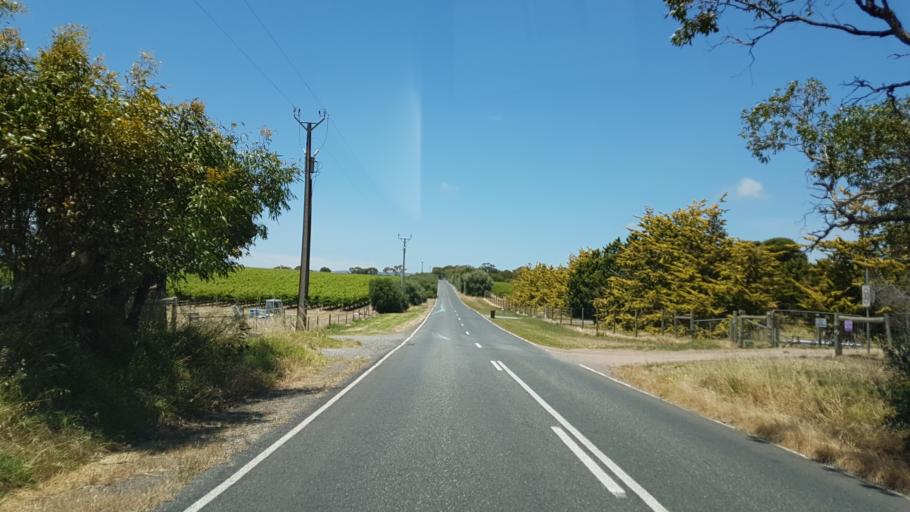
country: AU
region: South Australia
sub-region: Onkaparinga
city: Moana
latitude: -35.2322
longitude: 138.4995
